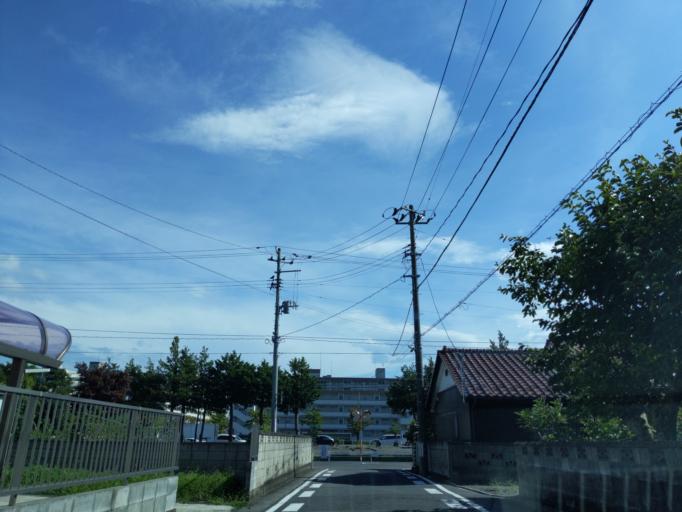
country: JP
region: Fukushima
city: Koriyama
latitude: 37.4114
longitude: 140.3390
